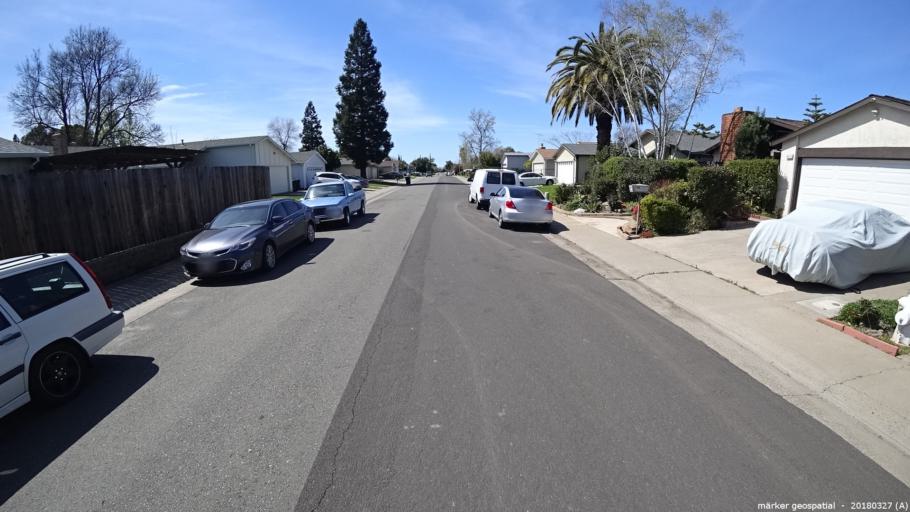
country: US
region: California
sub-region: Sacramento County
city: La Riviera
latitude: 38.5488
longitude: -121.3400
